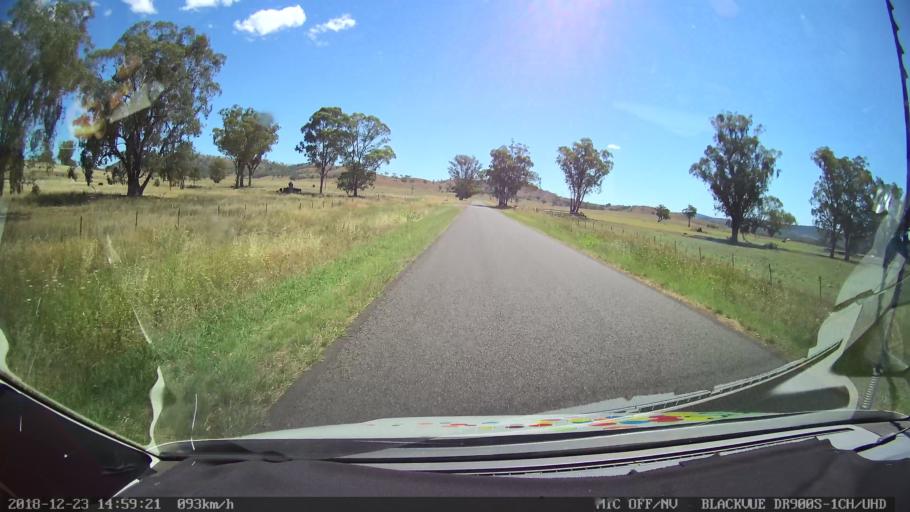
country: AU
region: New South Wales
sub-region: Tamworth Municipality
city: Manilla
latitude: -30.7232
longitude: 150.8018
